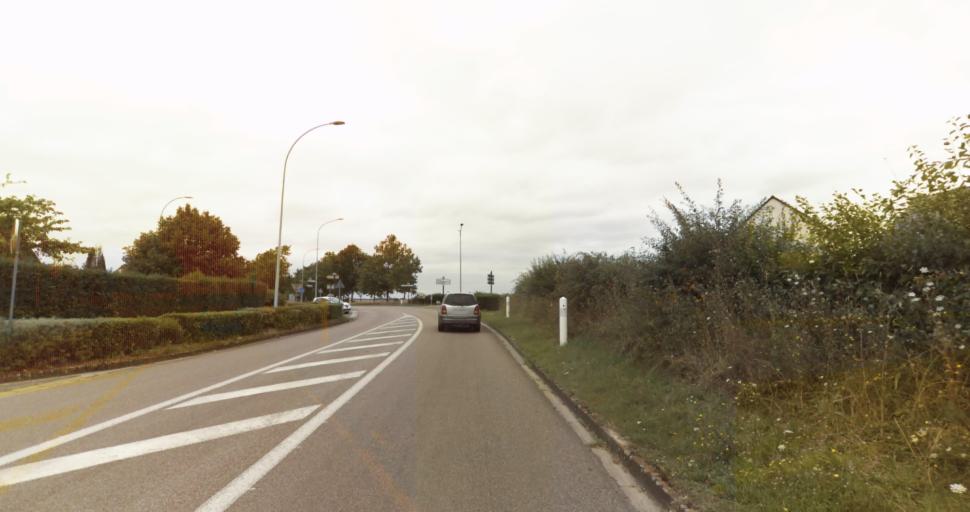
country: FR
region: Haute-Normandie
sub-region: Departement de l'Eure
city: Marcilly-sur-Eure
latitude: 48.9099
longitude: 1.2827
